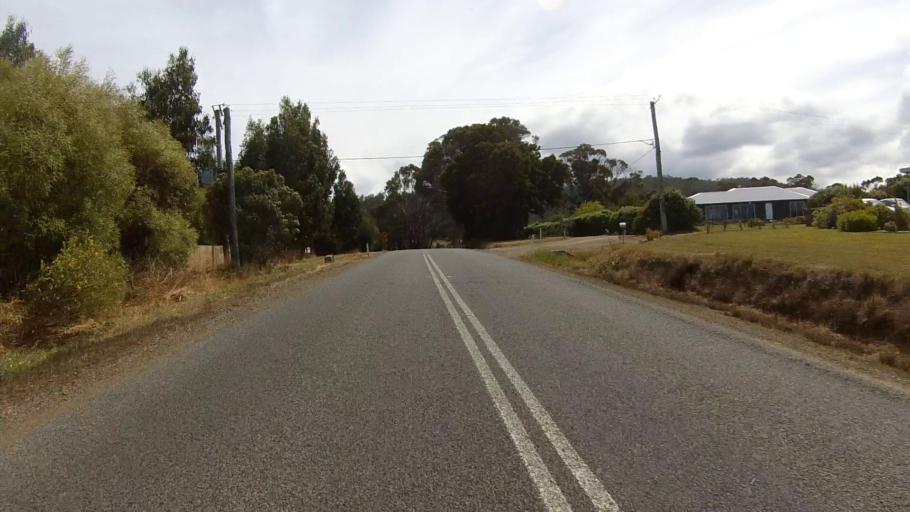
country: AU
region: Tasmania
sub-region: Huon Valley
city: Cygnet
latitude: -43.1893
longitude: 147.1004
